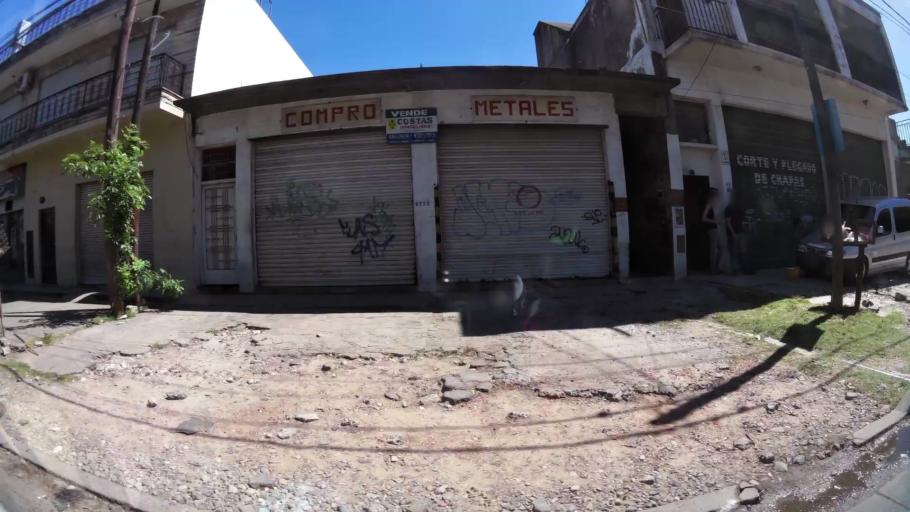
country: AR
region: Buenos Aires
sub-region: Partido de General San Martin
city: General San Martin
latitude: -34.5130
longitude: -58.5739
